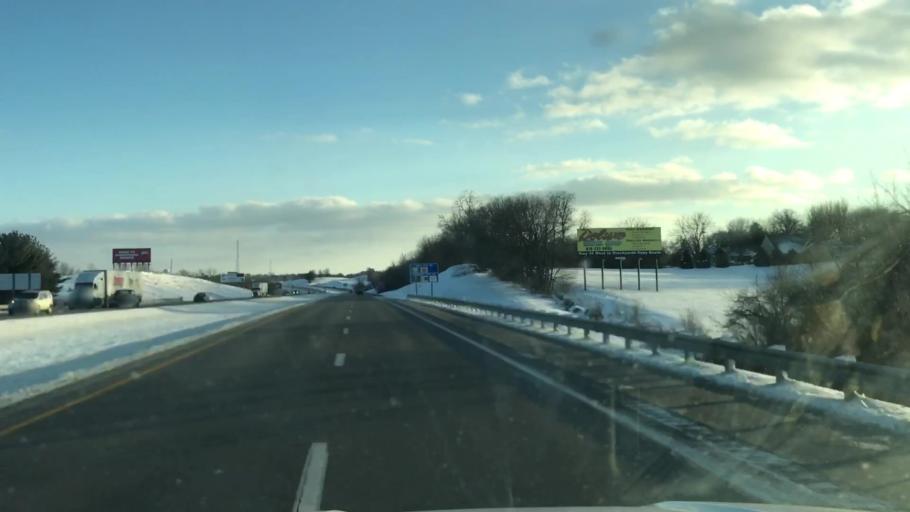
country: US
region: Missouri
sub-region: Andrew County
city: Country Club Village
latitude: 39.8286
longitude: -94.8055
